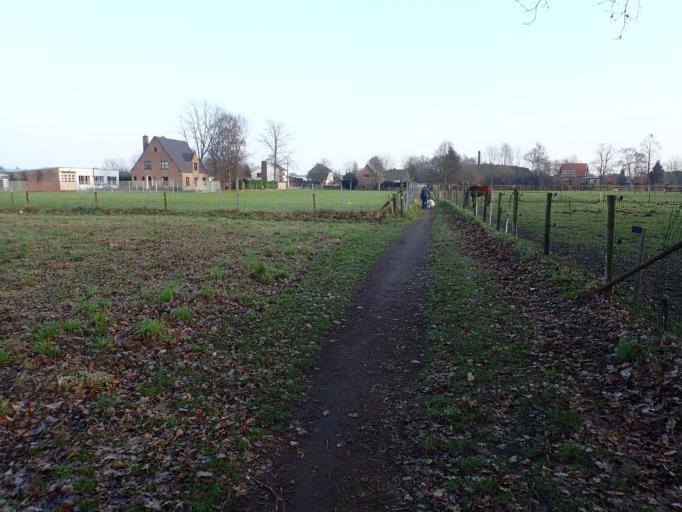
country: BE
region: Flanders
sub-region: Provincie Antwerpen
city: Borsbeek
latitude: 51.2042
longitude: 4.5029
